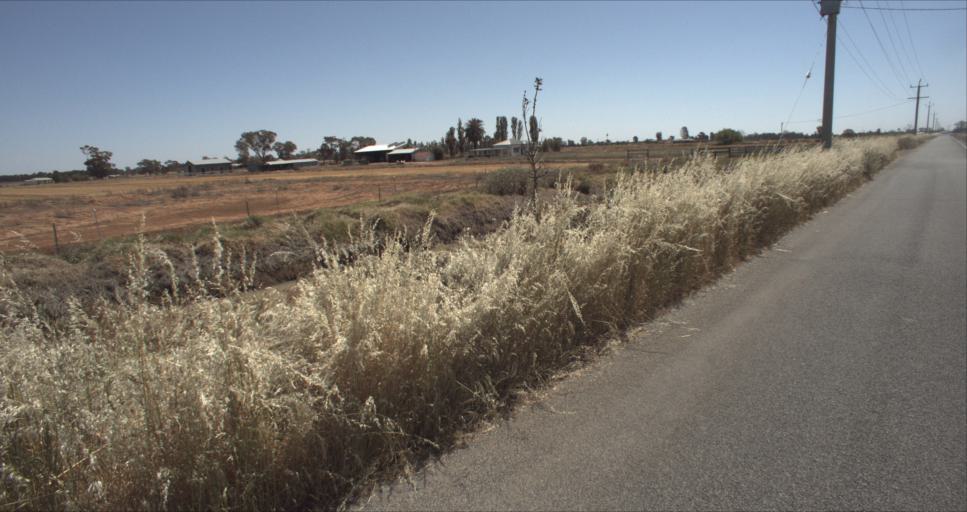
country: AU
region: New South Wales
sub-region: Leeton
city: Leeton
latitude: -34.5128
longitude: 146.4297
